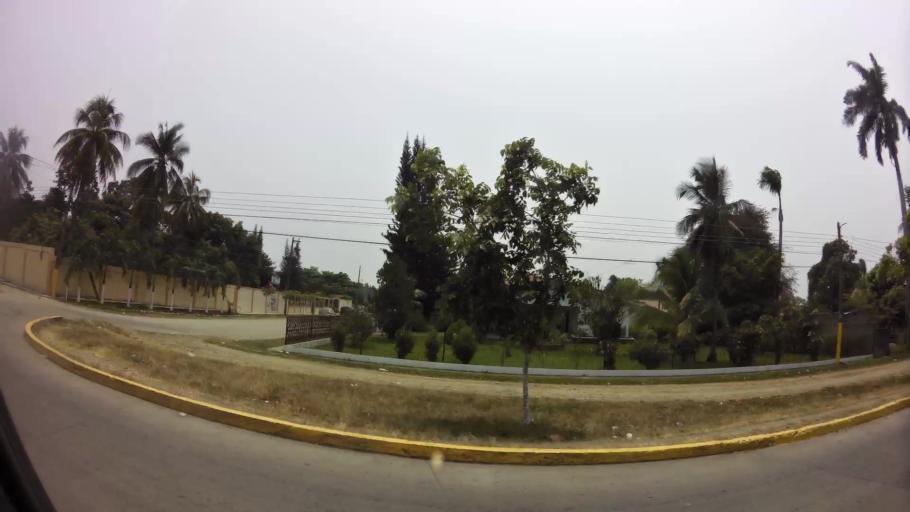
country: HN
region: Yoro
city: El Progreso
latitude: 15.3988
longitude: -87.8132
